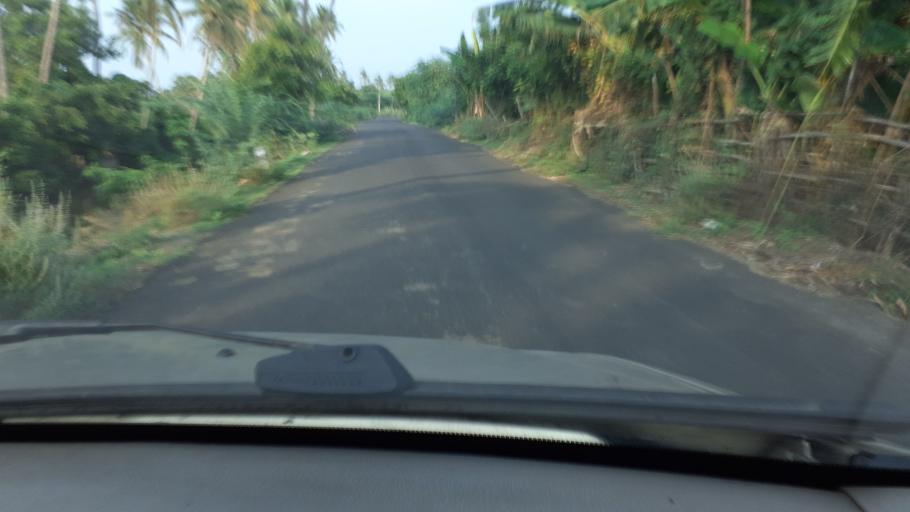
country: IN
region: Tamil Nadu
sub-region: Thoothukkudi
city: Alwar Tirunagari
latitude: 8.5995
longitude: 77.9748
